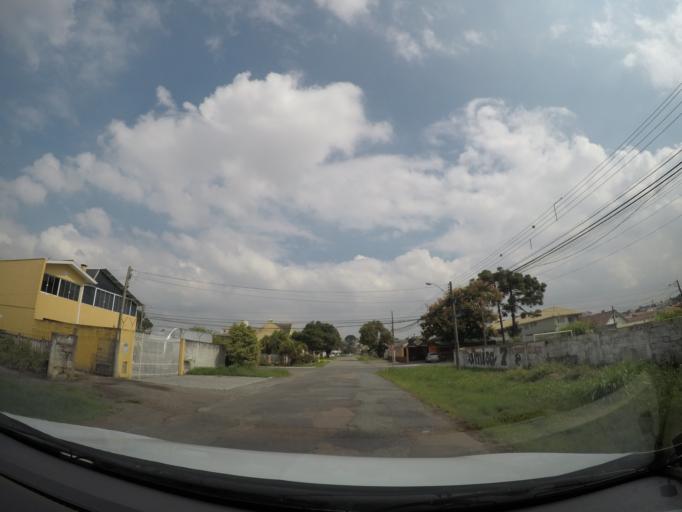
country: BR
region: Parana
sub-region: Sao Jose Dos Pinhais
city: Sao Jose dos Pinhais
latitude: -25.4915
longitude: -49.2517
